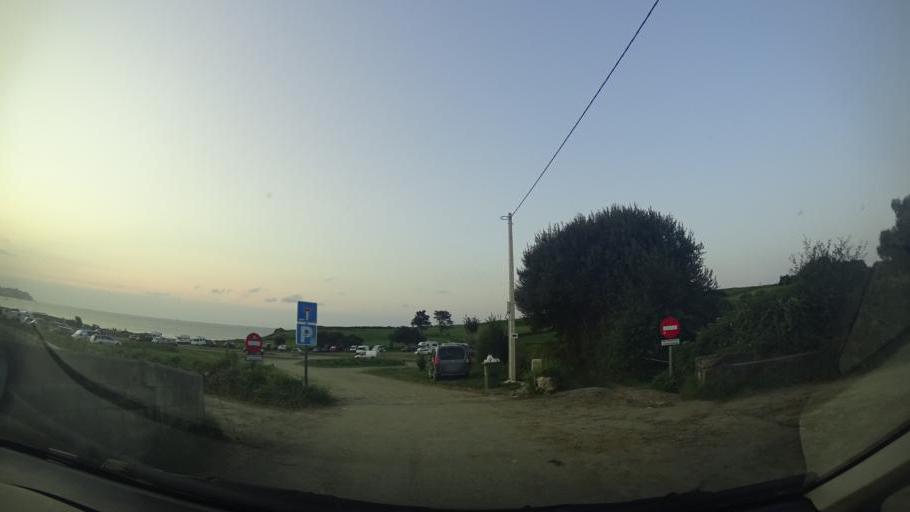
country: ES
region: Asturias
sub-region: Province of Asturias
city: Colunga
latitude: 43.4722
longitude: -5.2035
